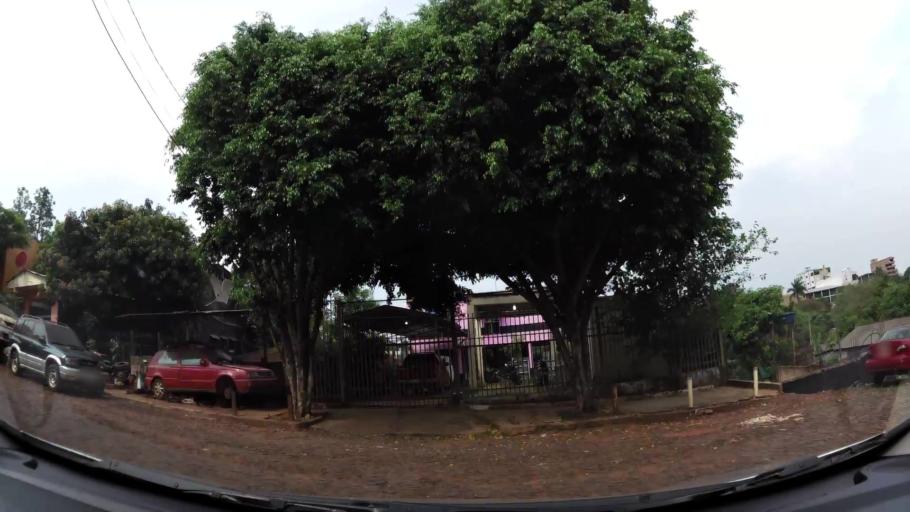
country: PY
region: Alto Parana
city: Presidente Franco
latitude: -25.5348
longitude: -54.6087
